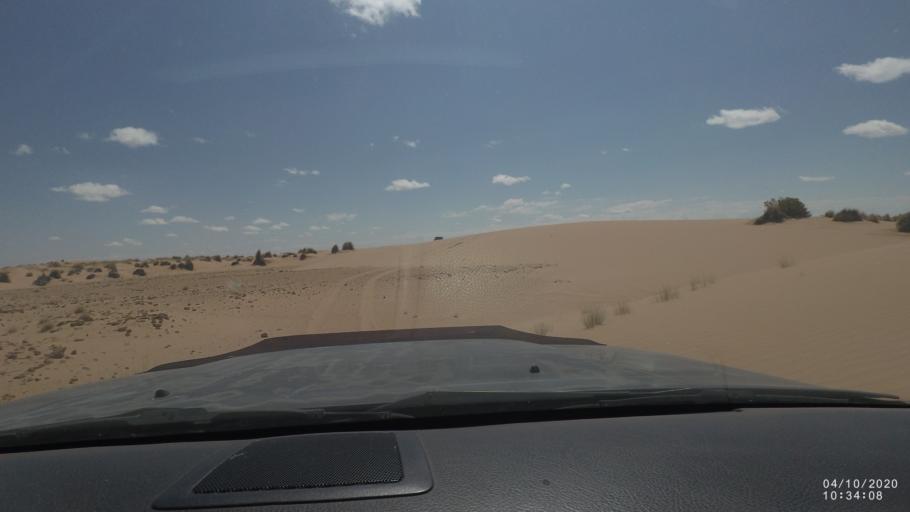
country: BO
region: Oruro
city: Poopo
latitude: -18.7053
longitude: -67.4781
